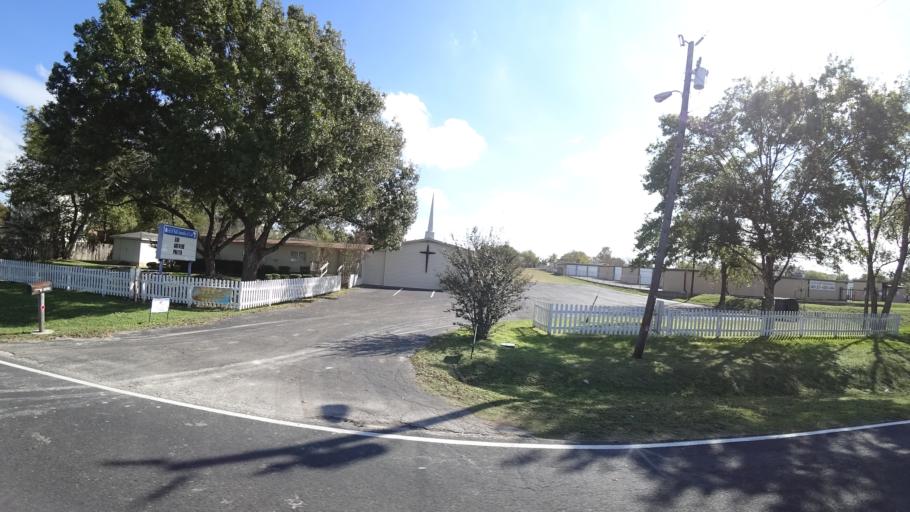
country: US
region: Texas
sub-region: Travis County
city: Windemere
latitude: 30.4547
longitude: -97.6525
